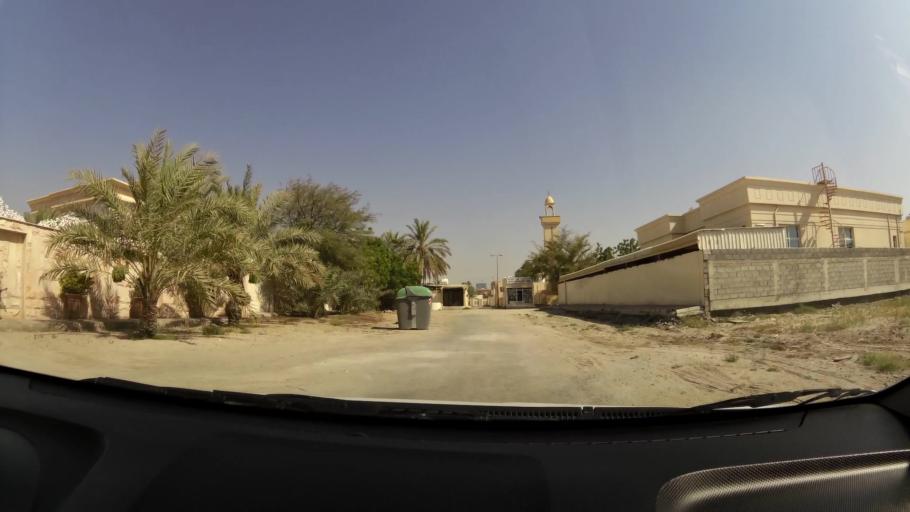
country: AE
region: Ajman
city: Ajman
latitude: 25.4165
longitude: 55.4668
